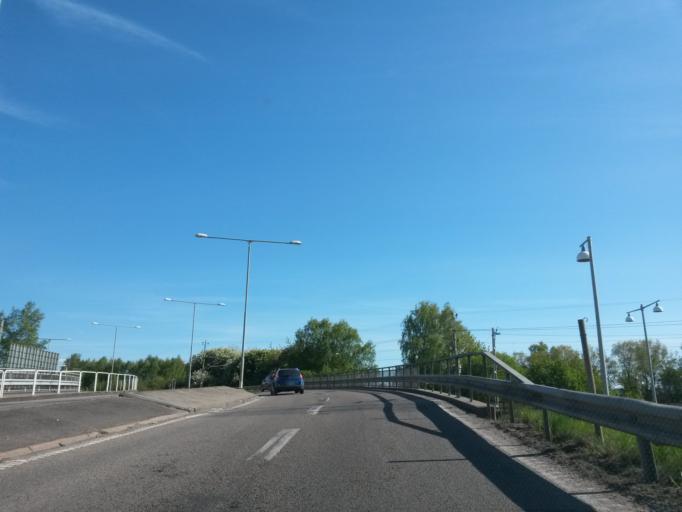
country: SE
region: Vaestra Goetaland
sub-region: Goteborg
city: Goeteborg
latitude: 57.7267
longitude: 11.9695
